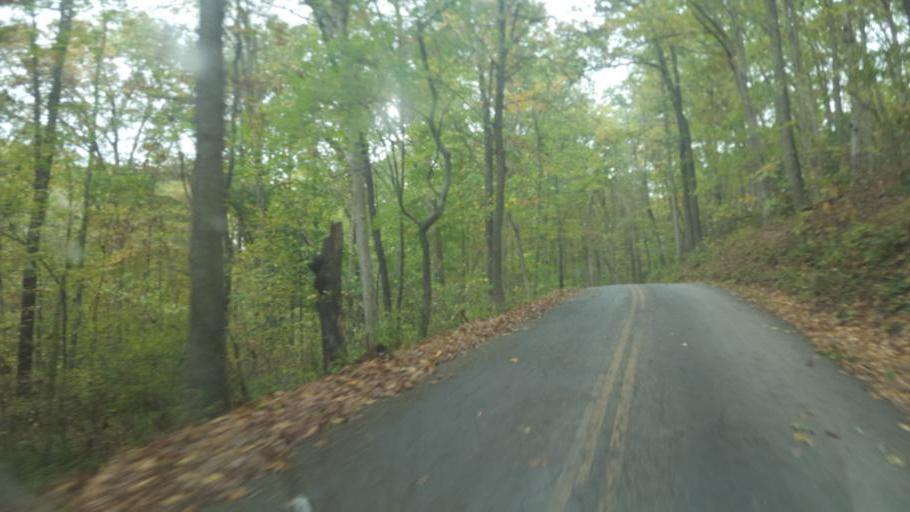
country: US
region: Ohio
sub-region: Carroll County
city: Carrollton
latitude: 40.4673
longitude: -81.1425
